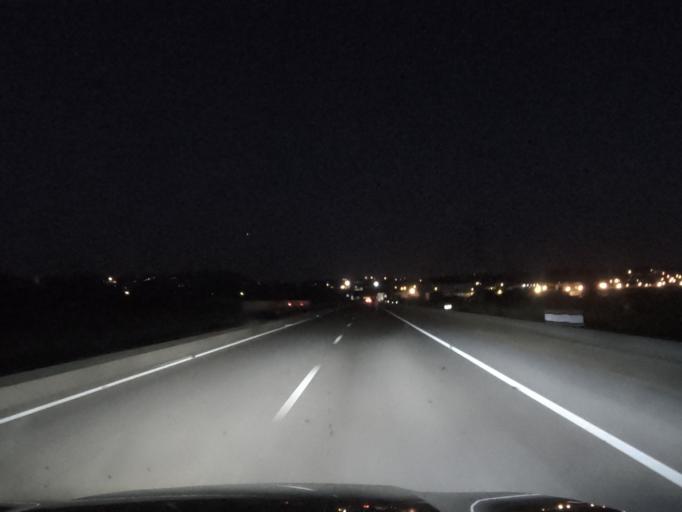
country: PT
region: Faro
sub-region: Loule
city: Loule
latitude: 37.1353
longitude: -8.0416
